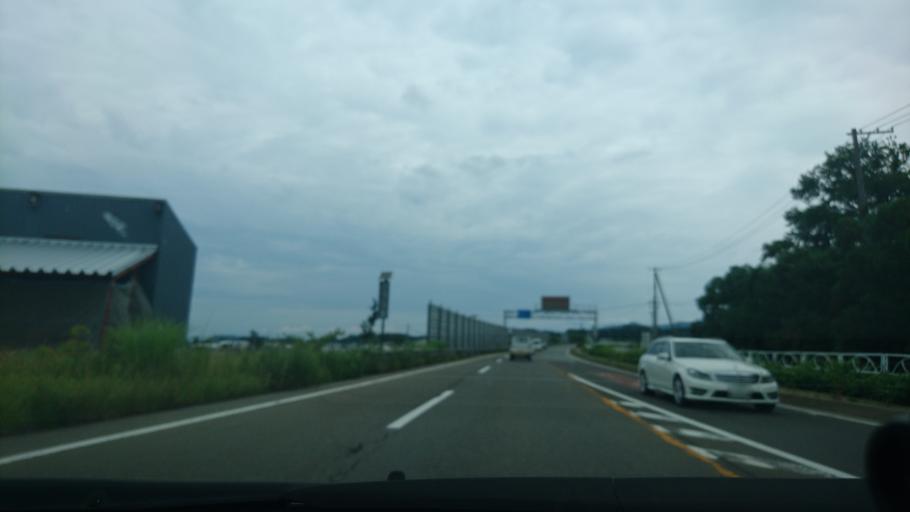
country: JP
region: Akita
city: Yokotemachi
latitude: 39.3277
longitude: 140.5550
